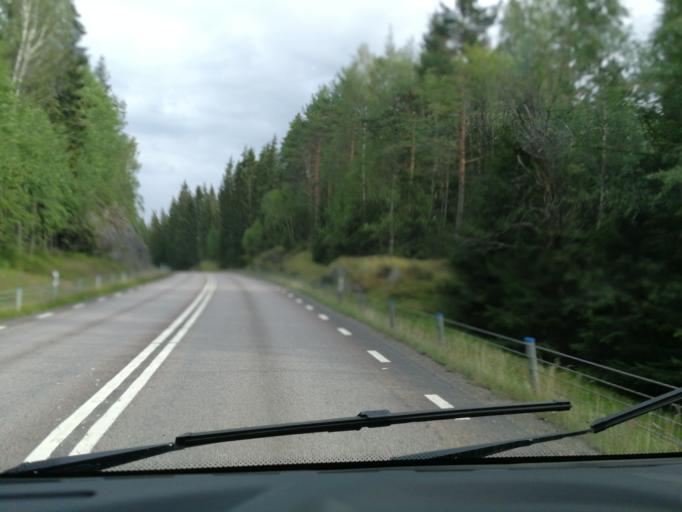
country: SE
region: Vaermland
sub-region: Arjangs Kommun
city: Toecksfors
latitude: 59.4985
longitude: 11.8802
